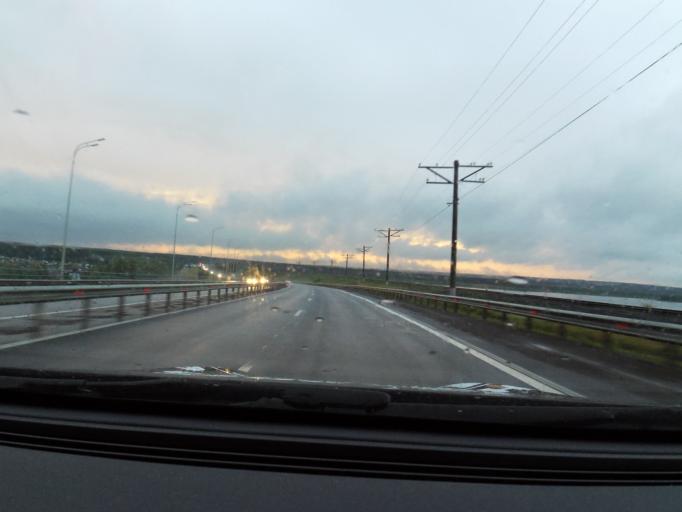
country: RU
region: Tatarstan
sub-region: Tukayevskiy Rayon
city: Naberezhnyye Chelny
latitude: 55.7086
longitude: 52.2745
